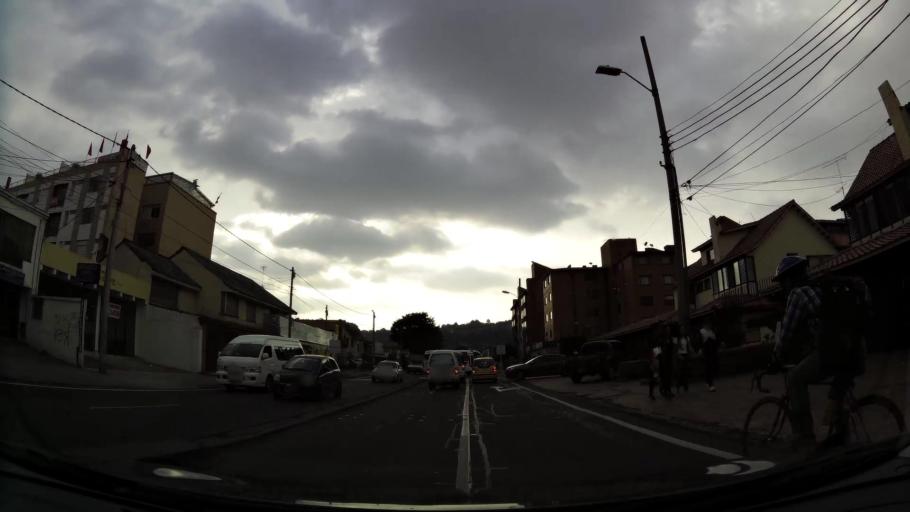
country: CO
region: Bogota D.C.
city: Barrio San Luis
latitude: 4.7187
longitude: -74.0702
